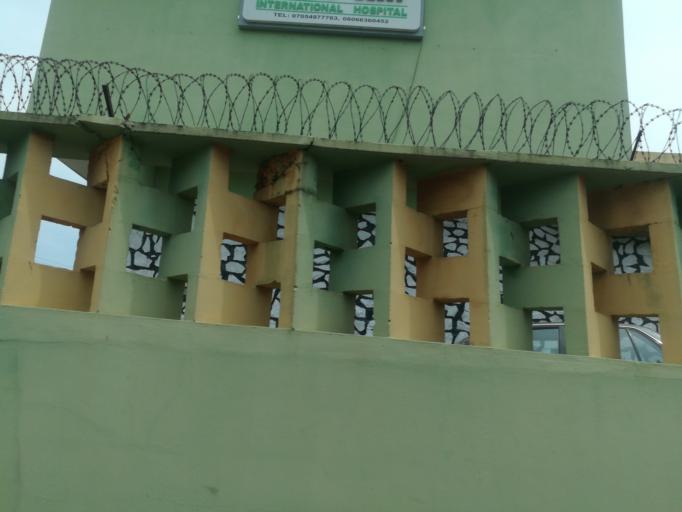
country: NG
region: Oyo
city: Ibadan
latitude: 7.4280
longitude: 3.9133
